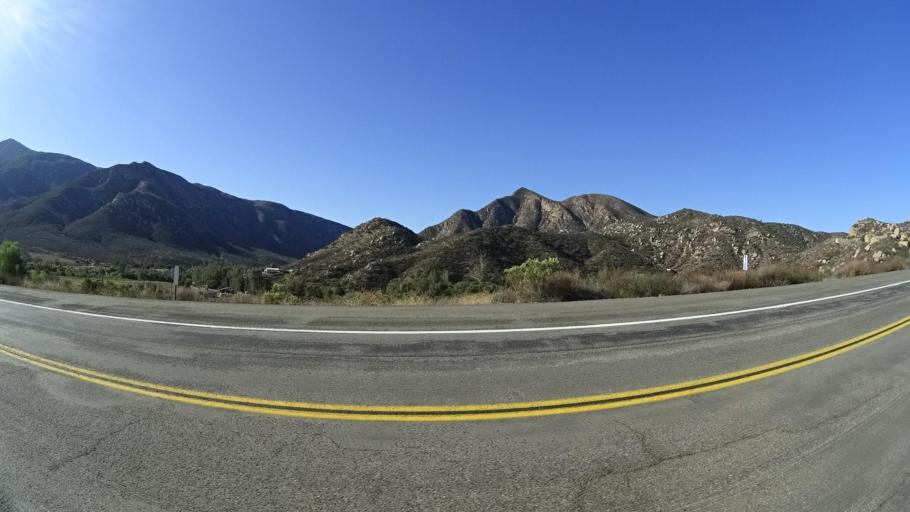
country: MX
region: Baja California
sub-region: Tecate
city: Lomas de Santa Anita
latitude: 32.6149
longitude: -116.7166
